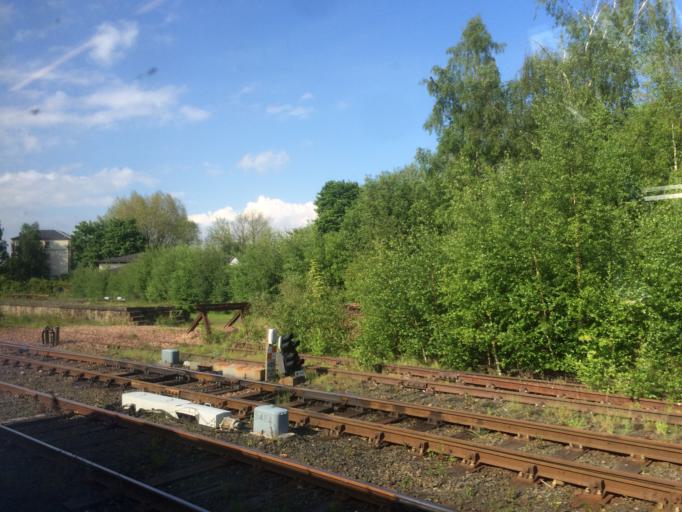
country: GB
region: Scotland
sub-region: Perth and Kinross
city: Perth
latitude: 56.3884
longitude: -3.4373
